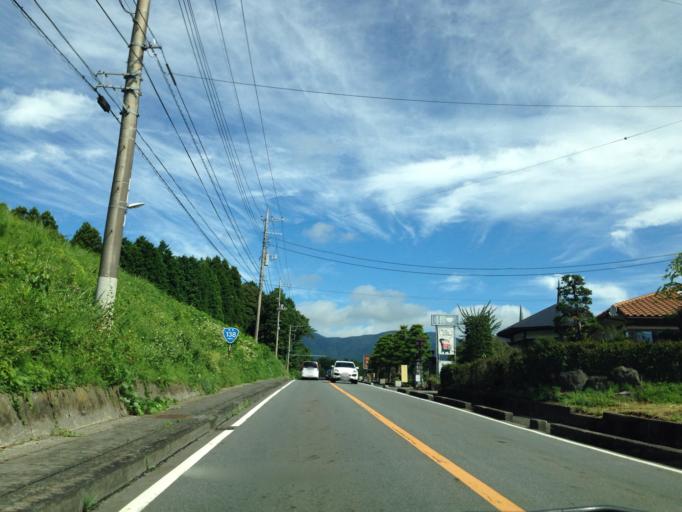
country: JP
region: Shizuoka
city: Gotemba
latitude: 35.3265
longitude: 138.9073
